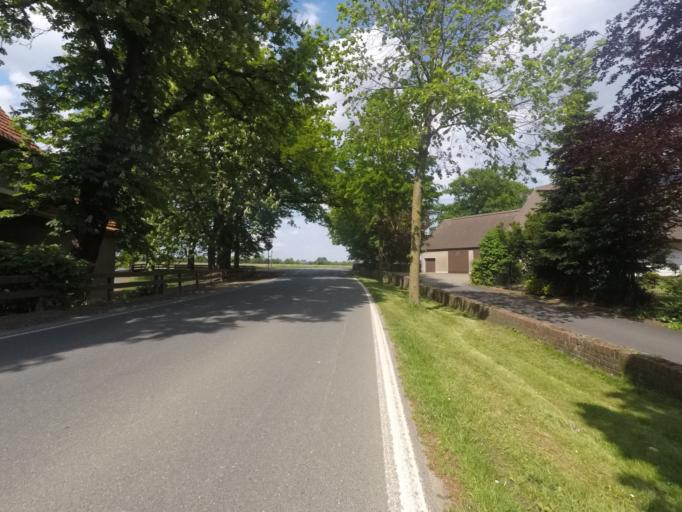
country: DE
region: North Rhine-Westphalia
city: Spenge
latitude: 52.1890
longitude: 8.5145
